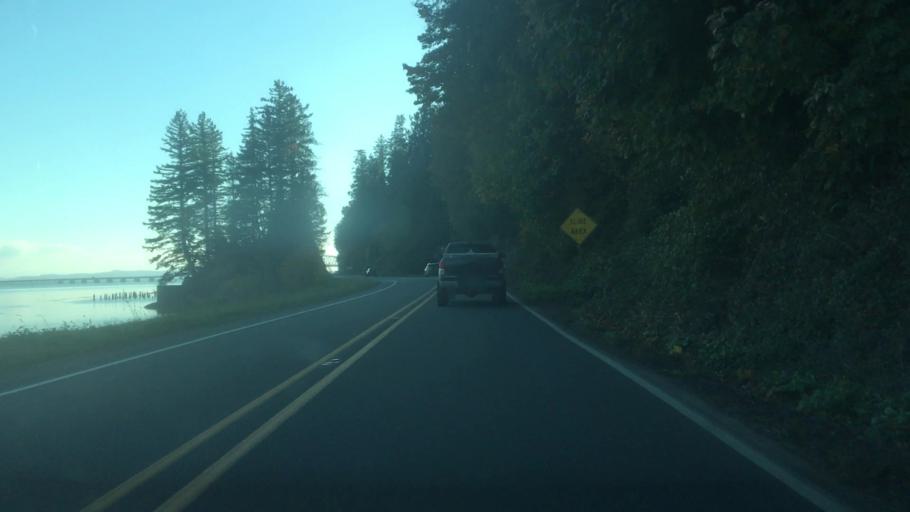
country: US
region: Oregon
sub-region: Clatsop County
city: Astoria
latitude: 46.2476
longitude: -123.8675
